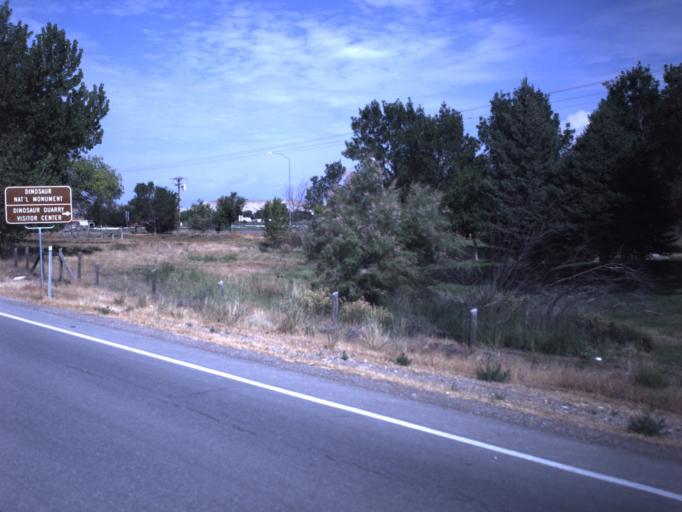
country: US
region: Utah
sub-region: Uintah County
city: Naples
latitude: 40.3699
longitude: -109.3440
